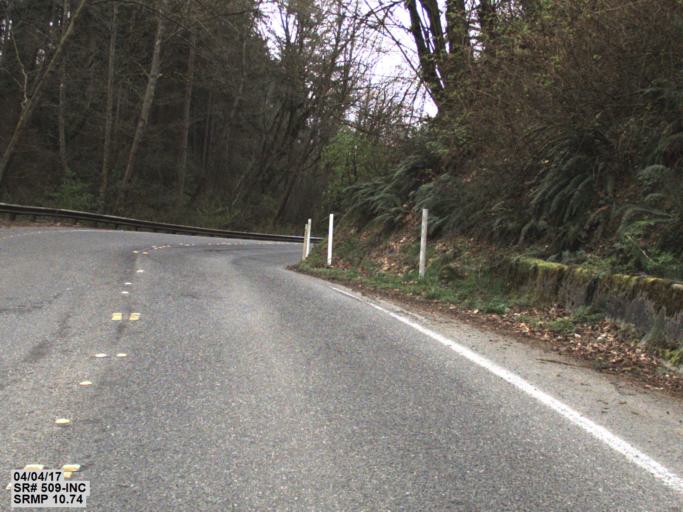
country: US
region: Washington
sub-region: King County
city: Federal Way
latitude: 47.3225
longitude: -122.3669
